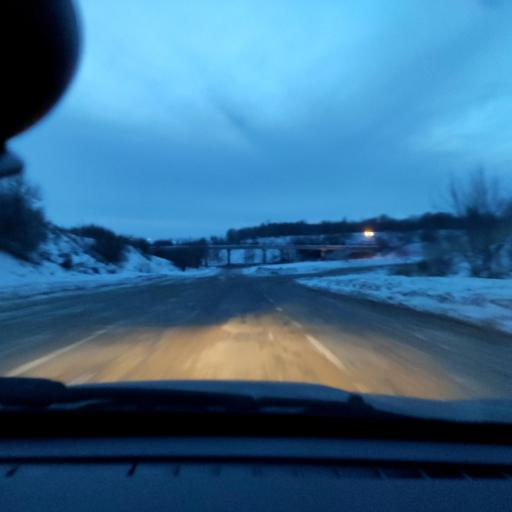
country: RU
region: Samara
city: Tol'yatti
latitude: 53.4969
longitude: 49.2729
